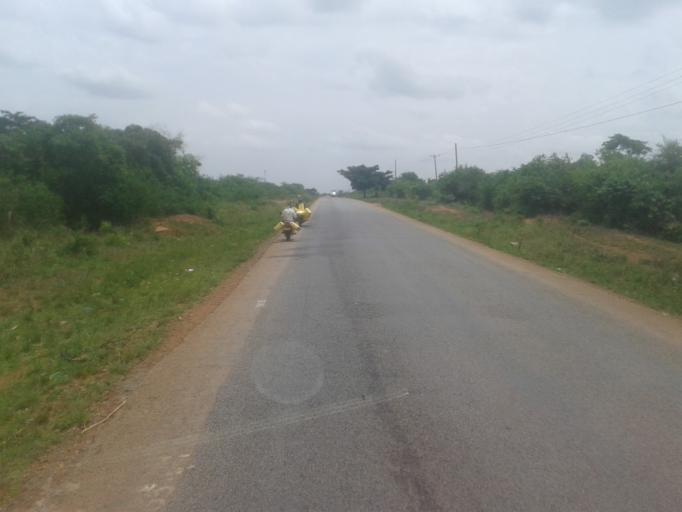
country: UG
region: Western Region
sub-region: Kiryandongo District
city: Masindi Port
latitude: 1.4843
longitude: 32.1377
